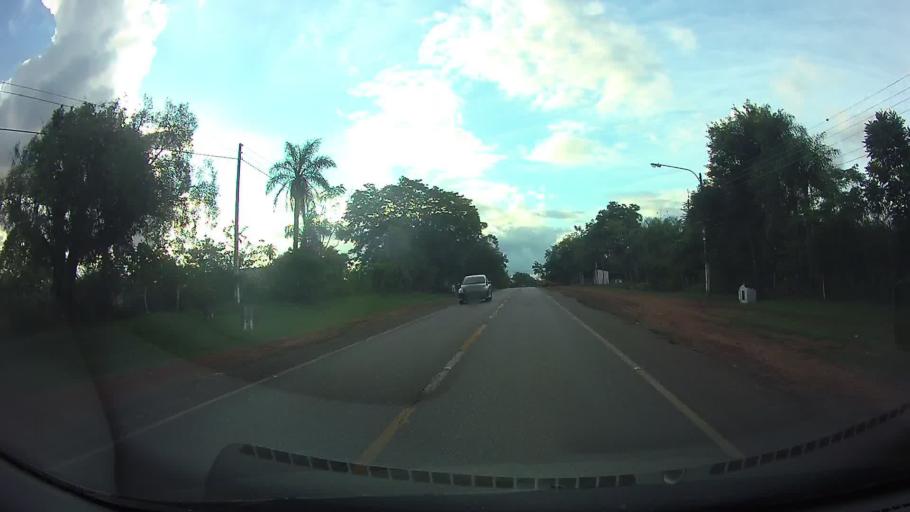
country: PY
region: Paraguari
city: Ybycui
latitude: -26.0129
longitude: -57.0321
